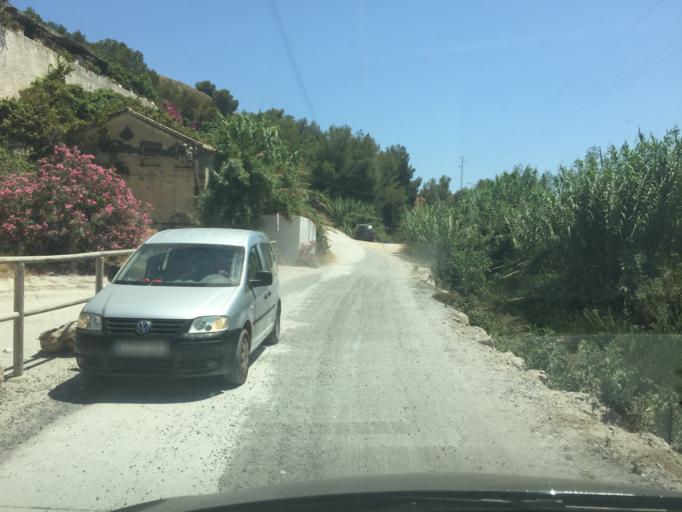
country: ES
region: Andalusia
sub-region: Provincia de Malaga
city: Nerja
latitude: 36.7712
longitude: -3.8782
